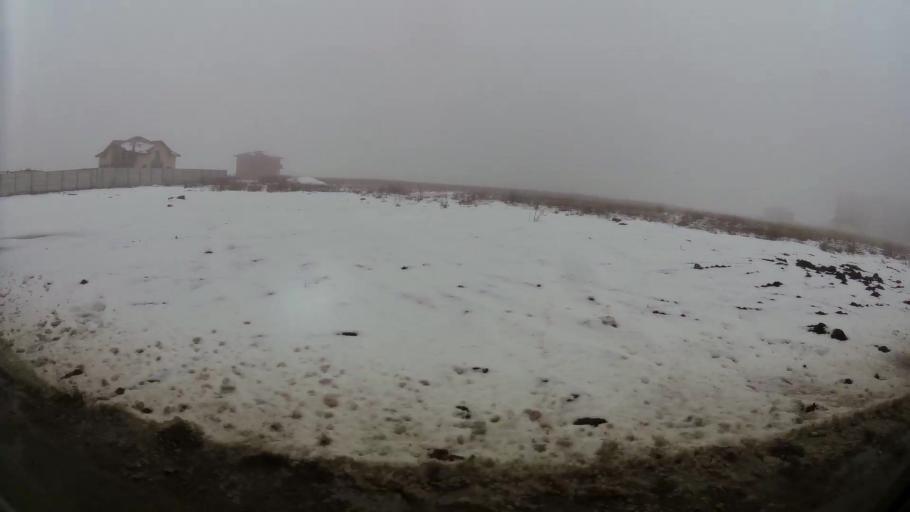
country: RO
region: Ilfov
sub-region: Comuna Chiajna
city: Chiajna
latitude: 44.4486
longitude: 25.9758
